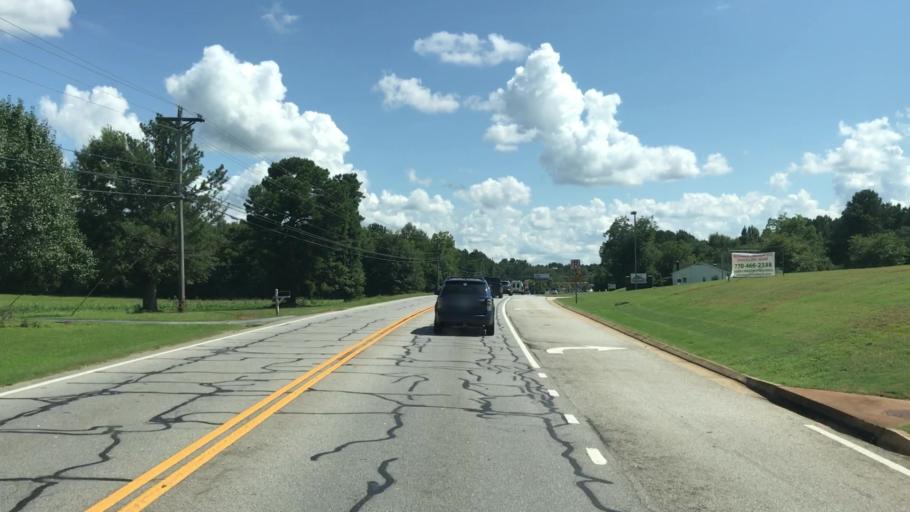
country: US
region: Georgia
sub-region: Walton County
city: Loganville
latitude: 33.8098
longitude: -83.8739
